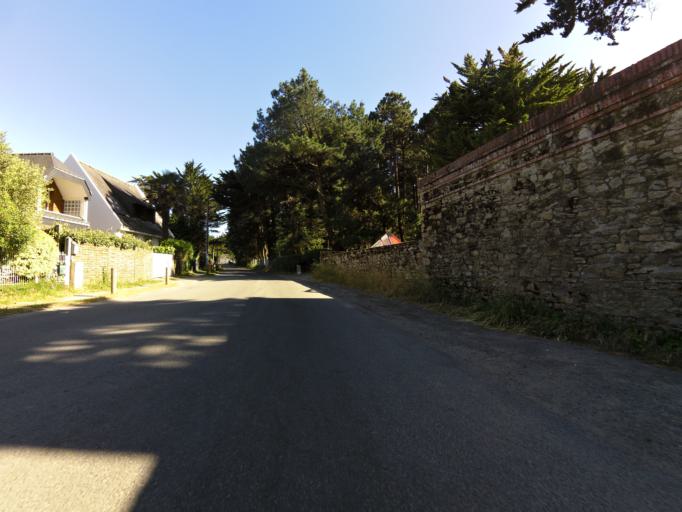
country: FR
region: Brittany
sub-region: Departement du Morbihan
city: Penestin
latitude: 47.4668
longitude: -2.4889
